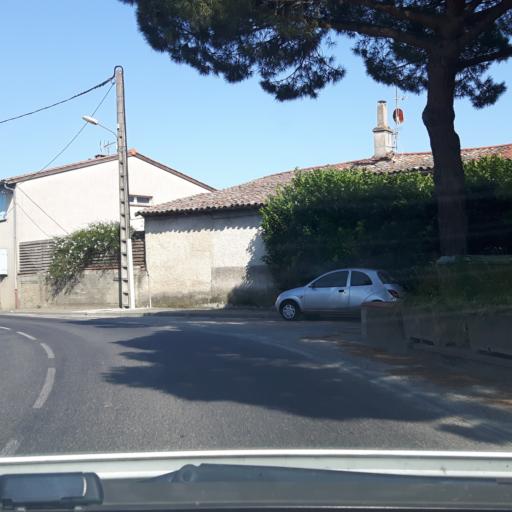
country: FR
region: Midi-Pyrenees
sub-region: Departement de la Haute-Garonne
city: Ondes
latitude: 43.7803
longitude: 1.3109
